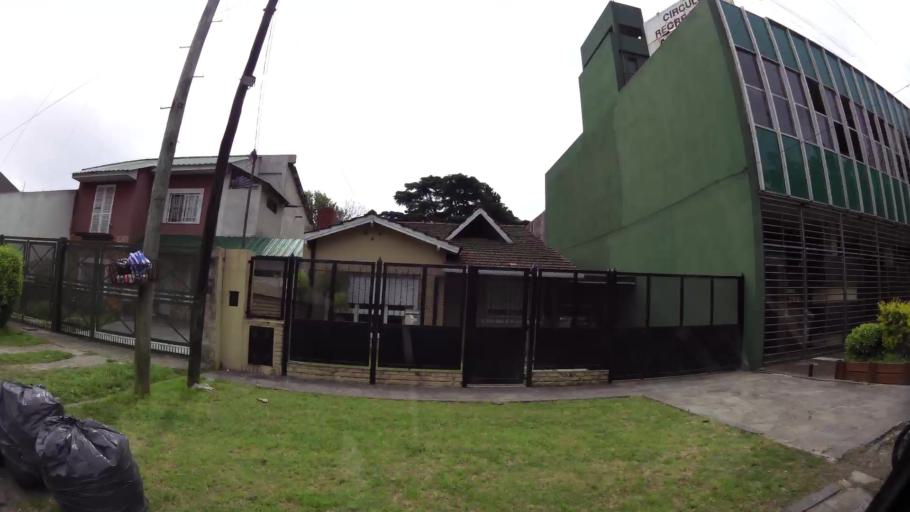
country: AR
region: Buenos Aires
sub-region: Partido de Quilmes
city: Quilmes
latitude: -34.7761
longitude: -58.2645
